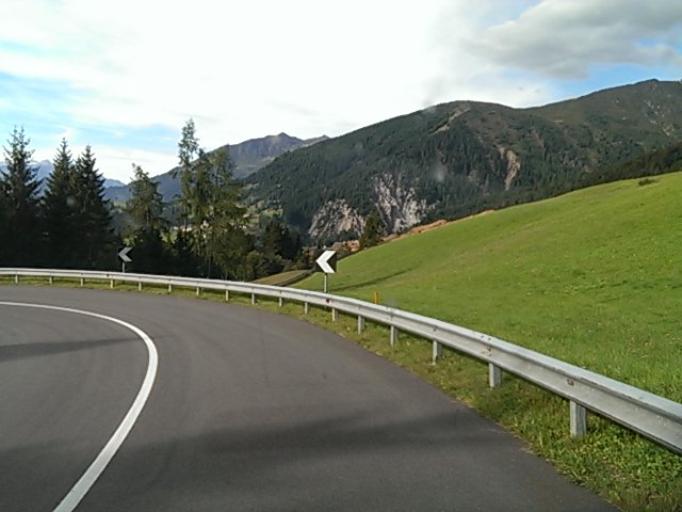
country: IT
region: Trentino-Alto Adige
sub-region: Bolzano
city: Proves - Proveis
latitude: 46.4918
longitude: 11.0372
